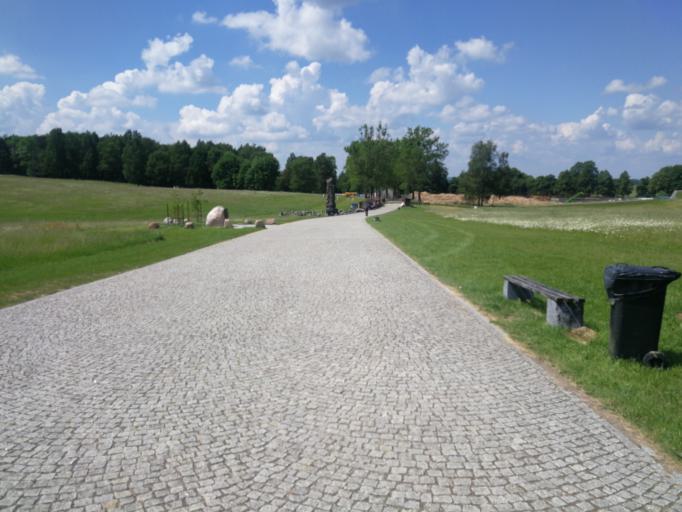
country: PL
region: Warmian-Masurian Voivodeship
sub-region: Powiat ostrodzki
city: Gierzwald
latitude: 53.4876
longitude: 20.1219
